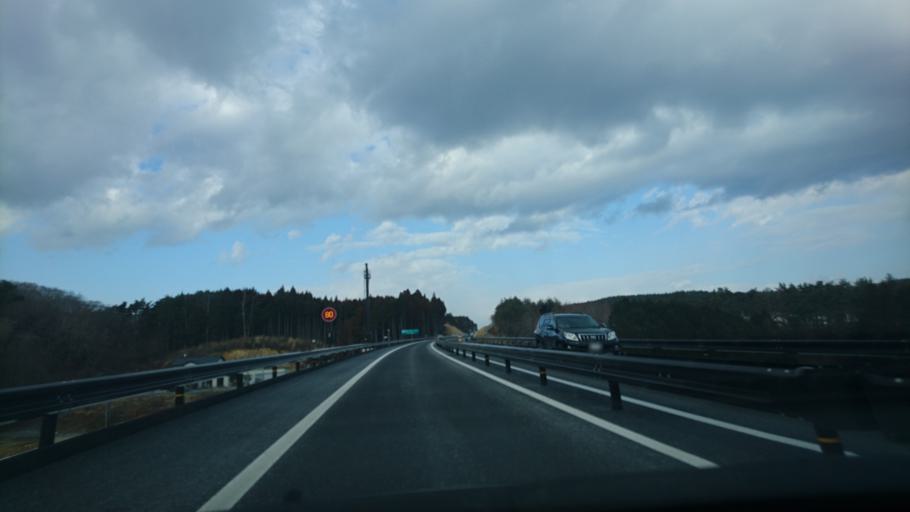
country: JP
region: Miyagi
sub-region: Oshika Gun
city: Onagawa Cho
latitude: 38.7230
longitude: 141.5128
